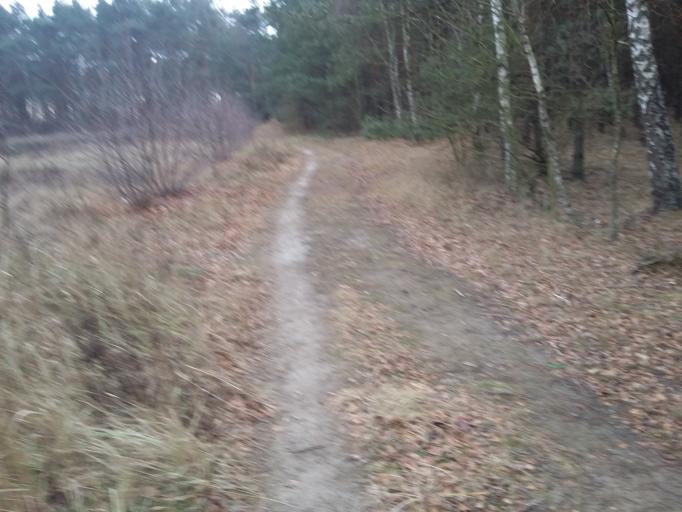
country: PL
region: Lodz Voivodeship
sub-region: Powiat pabianicki
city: Ksawerow
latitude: 51.7243
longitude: 19.3847
